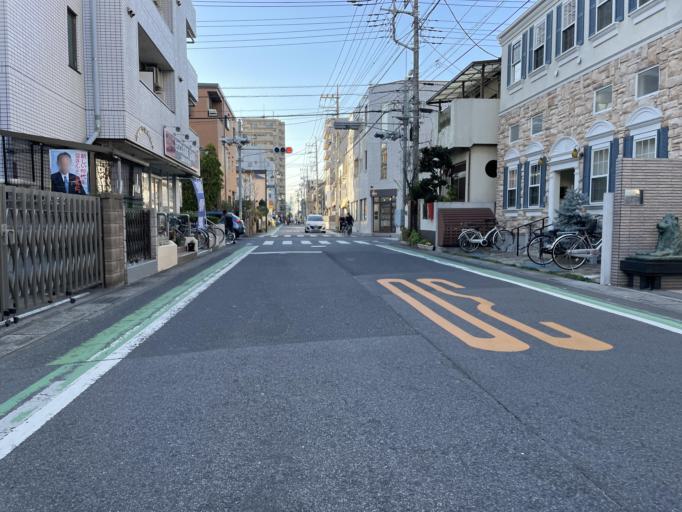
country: JP
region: Saitama
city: Soka
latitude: 35.8292
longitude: 139.8017
